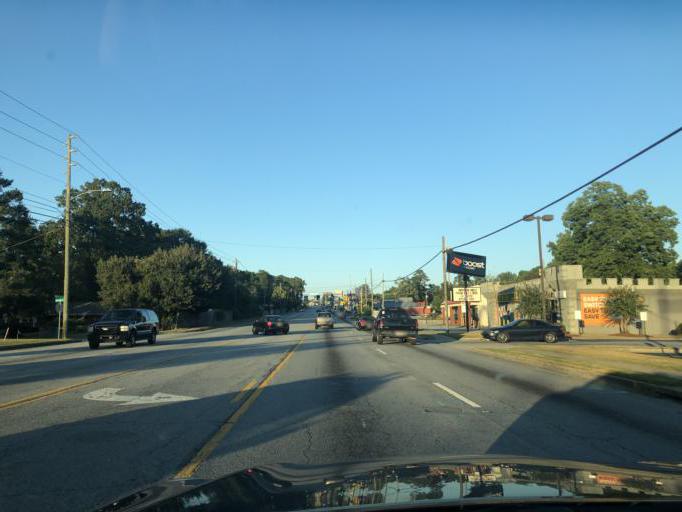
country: US
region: Georgia
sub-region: Muscogee County
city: Columbus
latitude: 32.4639
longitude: -84.9236
